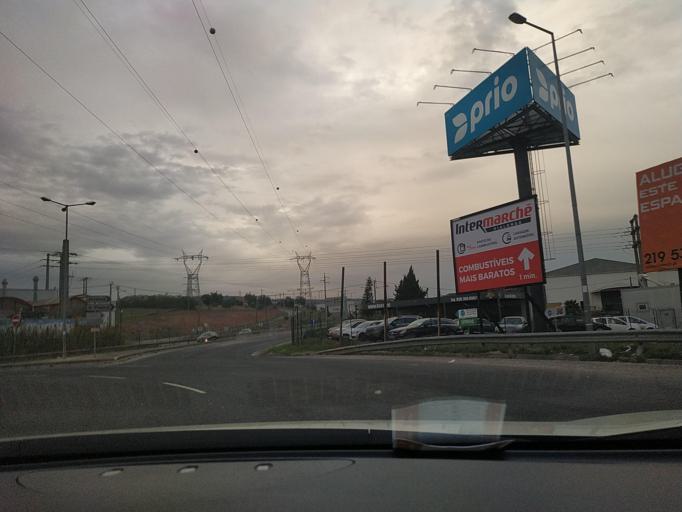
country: PT
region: Lisbon
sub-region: Loures
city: Santo Antao do Tojal
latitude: 38.8606
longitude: -9.1145
